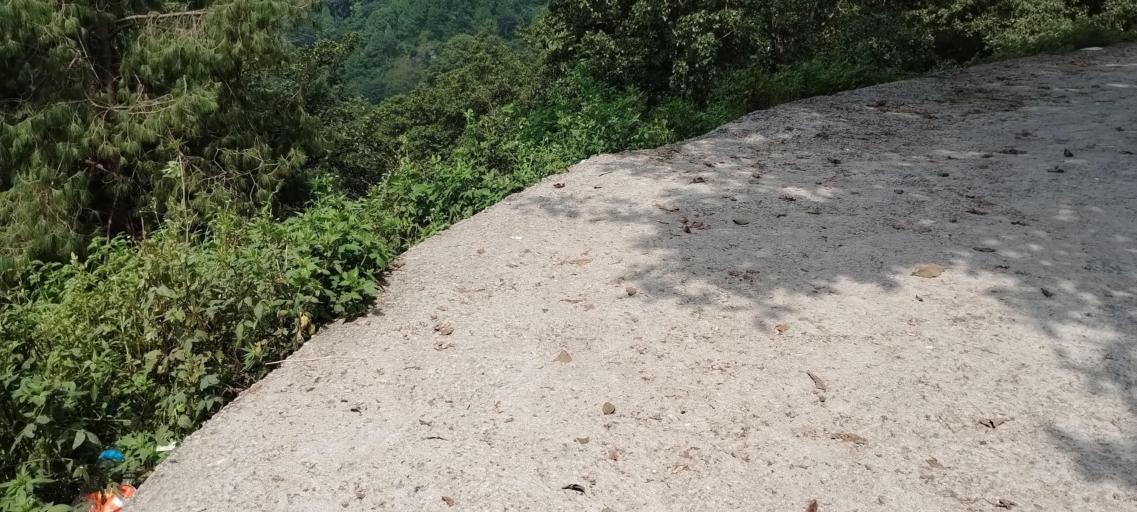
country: NP
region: Central Region
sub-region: Bagmati Zone
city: Kathmandu
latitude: 27.7893
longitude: 85.3604
